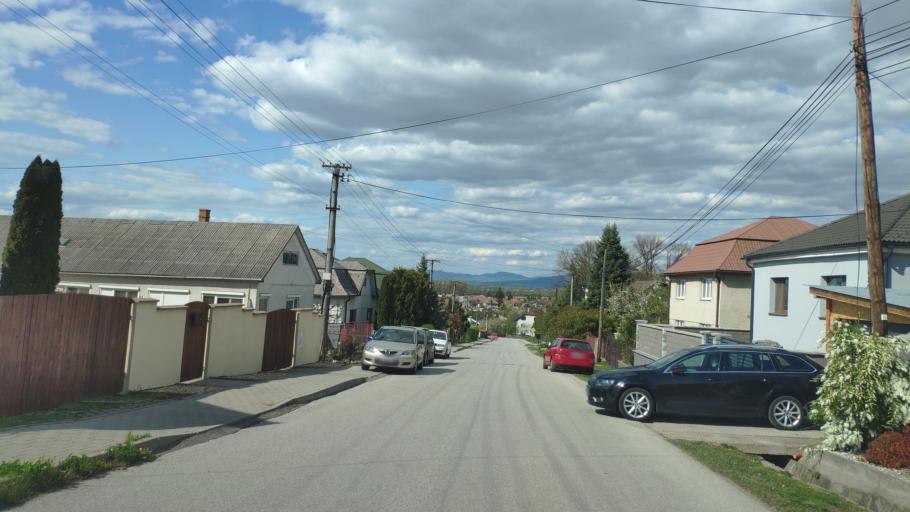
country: SK
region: Kosicky
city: Kosice
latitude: 48.6787
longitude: 21.4309
